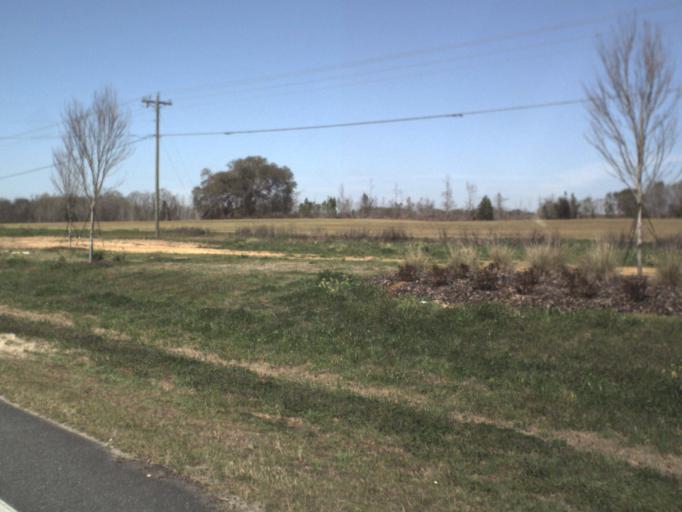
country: US
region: Florida
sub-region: Jackson County
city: Sneads
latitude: 30.7193
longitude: -85.0345
